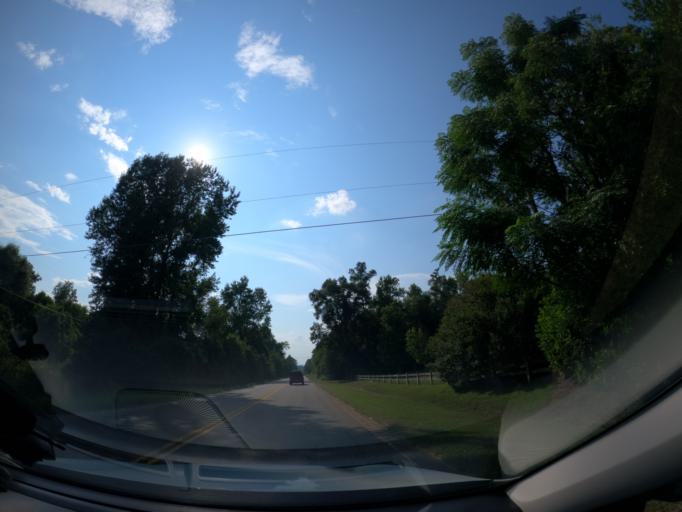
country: US
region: South Carolina
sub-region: Aiken County
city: Clearwater
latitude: 33.4234
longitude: -81.8619
